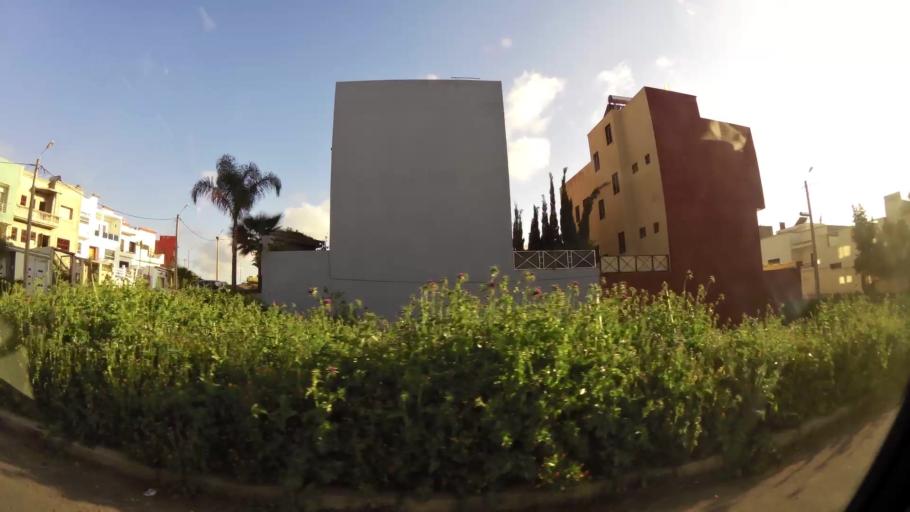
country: MA
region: Chaouia-Ouardigha
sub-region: Settat Province
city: Settat
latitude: 33.0085
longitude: -7.6063
